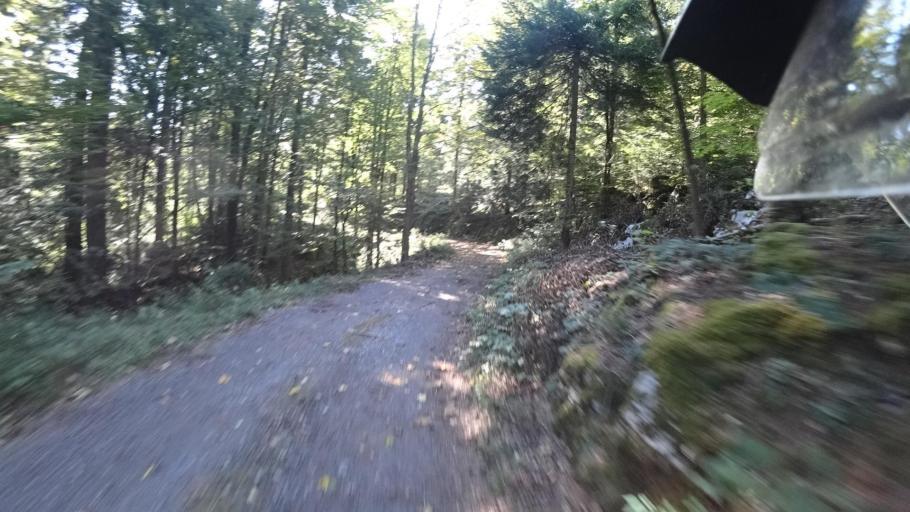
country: HR
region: Primorsko-Goranska
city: Vrbovsko
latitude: 45.2665
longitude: 15.1016
